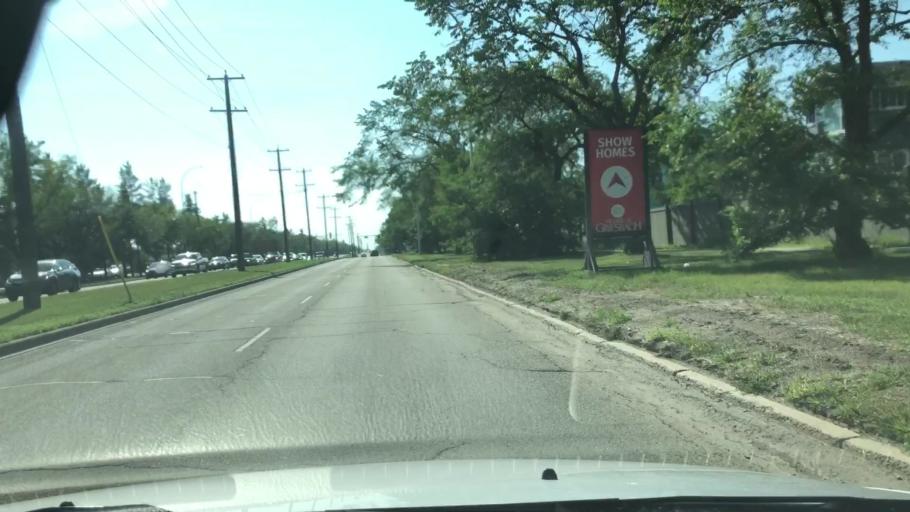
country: CA
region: Alberta
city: Edmonton
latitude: 53.5996
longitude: -113.5007
